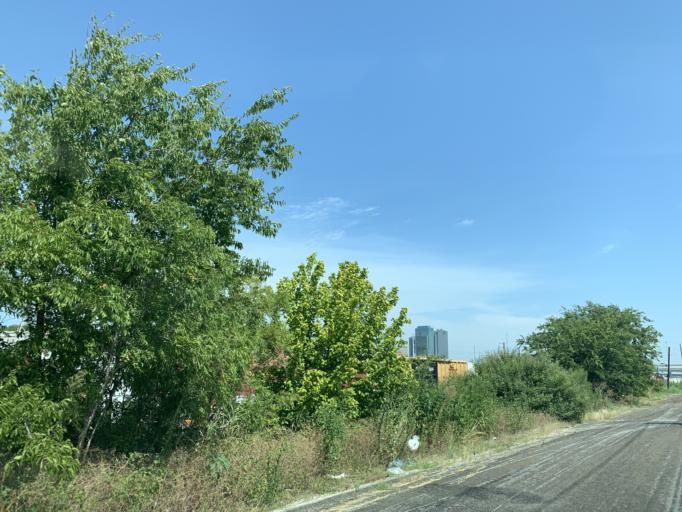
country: US
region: Texas
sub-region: Tarrant County
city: Fort Worth
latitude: 32.7387
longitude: -97.3215
